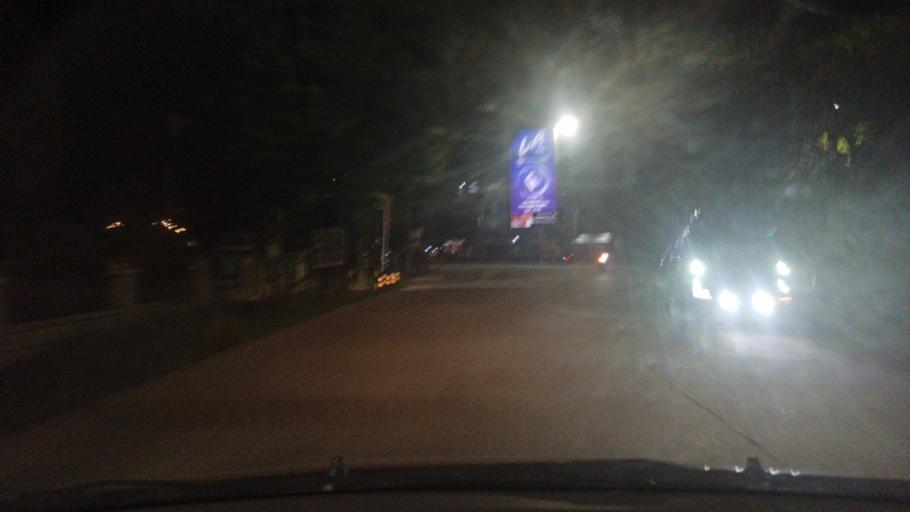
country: ID
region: South Sumatra
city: Plaju
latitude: -2.9501
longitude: 104.7855
